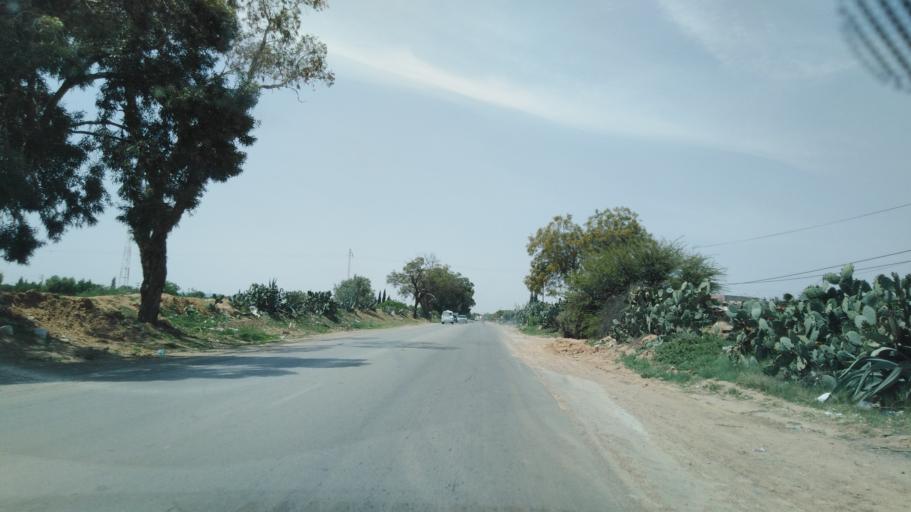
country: TN
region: Safaqis
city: Sfax
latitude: 34.7317
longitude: 10.5602
